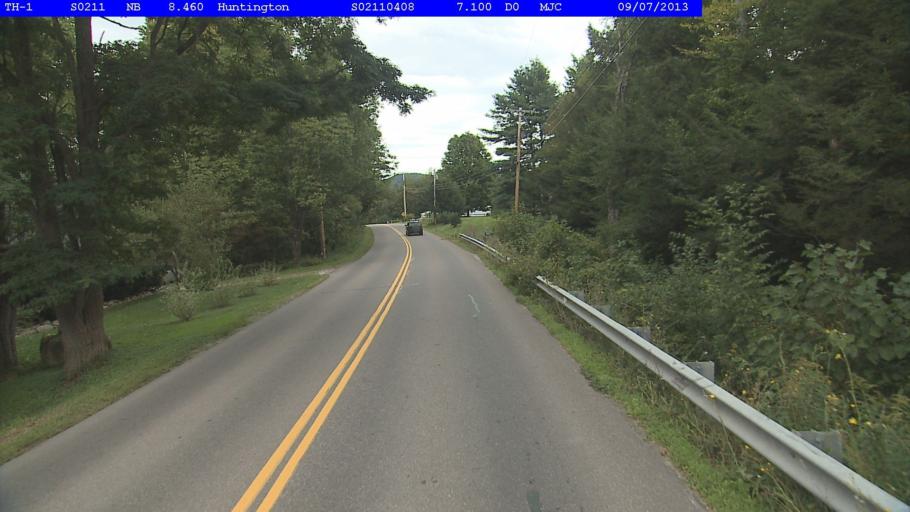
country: US
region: Vermont
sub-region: Chittenden County
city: Hinesburg
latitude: 44.3210
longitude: -72.9891
